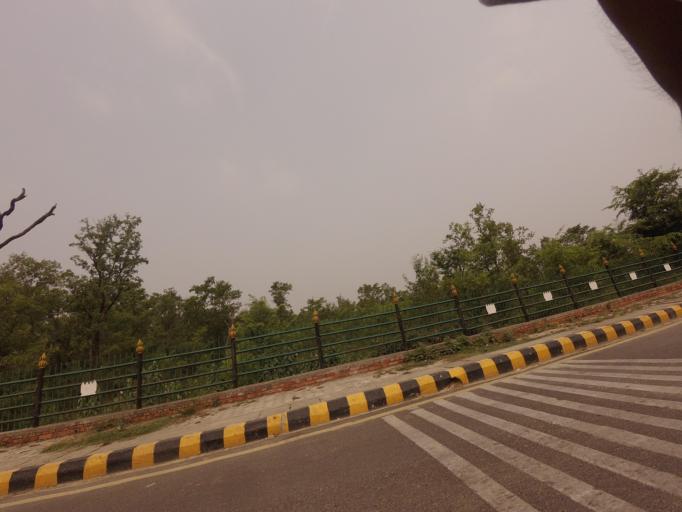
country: IN
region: Uttar Pradesh
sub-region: Maharajganj
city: Nautanwa
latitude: 27.4904
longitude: 83.2843
